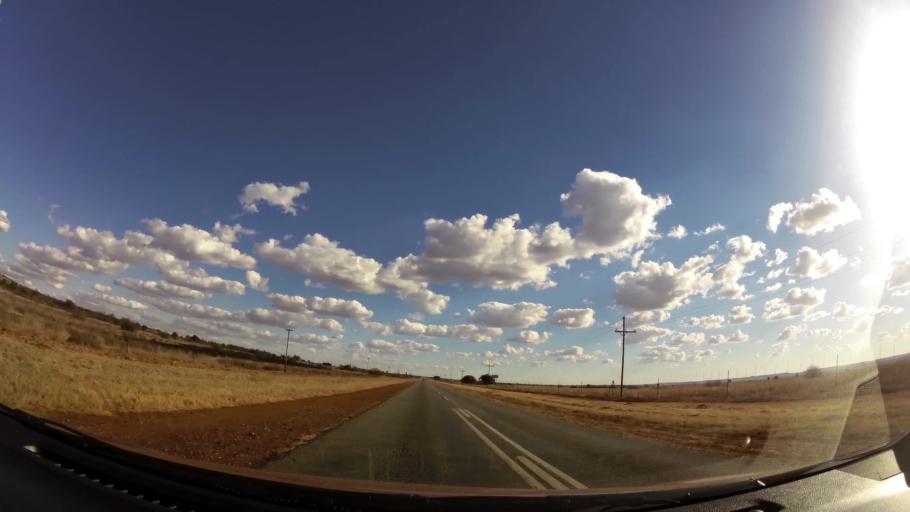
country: ZA
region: Gauteng
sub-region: West Rand District Municipality
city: Carletonville
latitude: -26.4145
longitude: 27.2332
